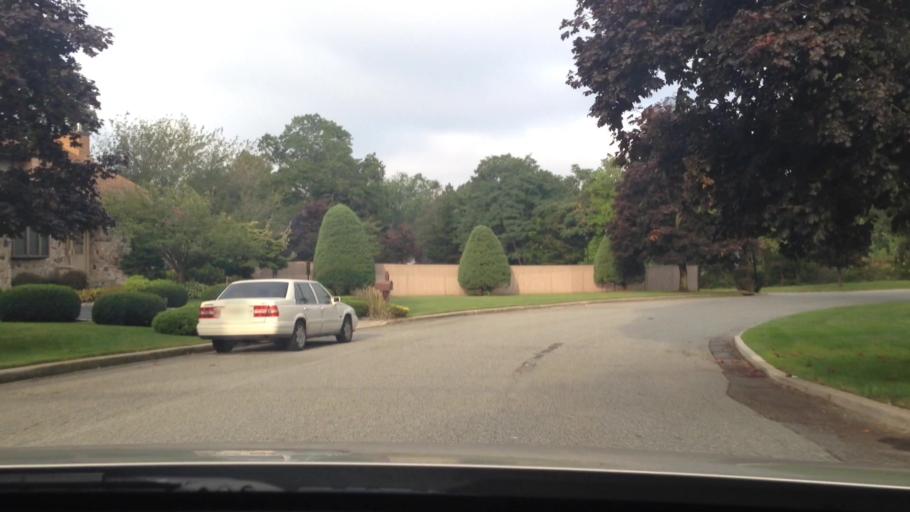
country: US
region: New York
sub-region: Suffolk County
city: Farmingville
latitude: 40.8386
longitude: -73.0499
